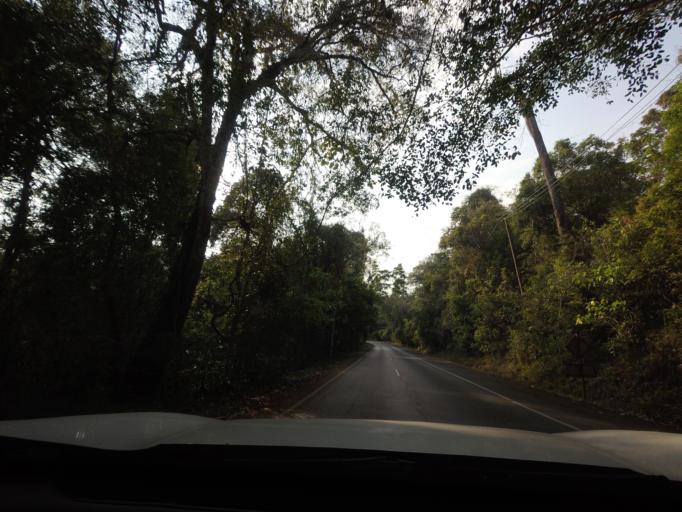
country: TH
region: Nakhon Nayok
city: Nakhon Nayok
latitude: 14.4203
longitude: 101.3864
